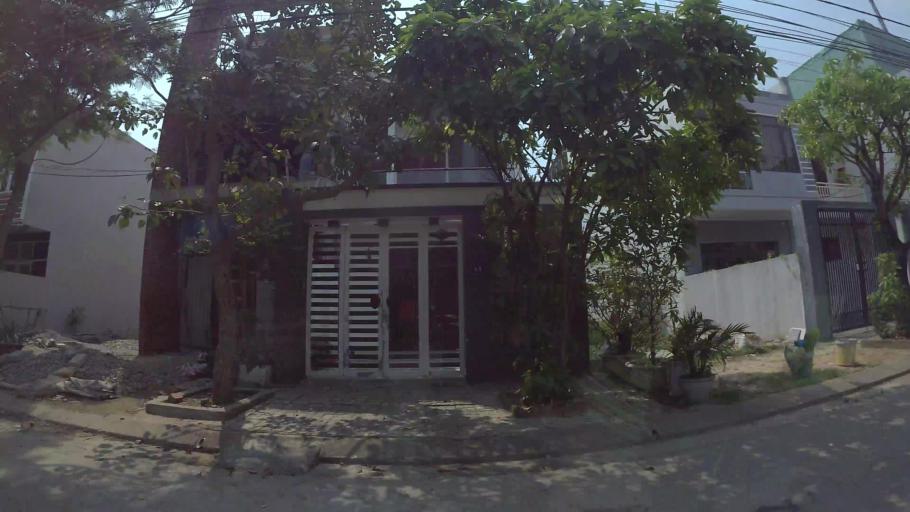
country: VN
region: Da Nang
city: Cam Le
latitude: 16.0038
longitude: 108.2098
